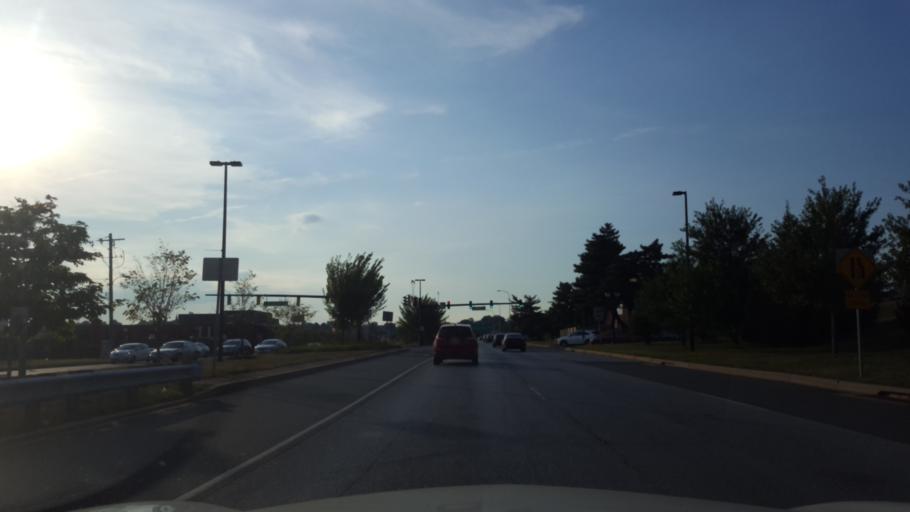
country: US
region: Delaware
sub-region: New Castle County
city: Wilmington
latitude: 39.7397
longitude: -75.5566
